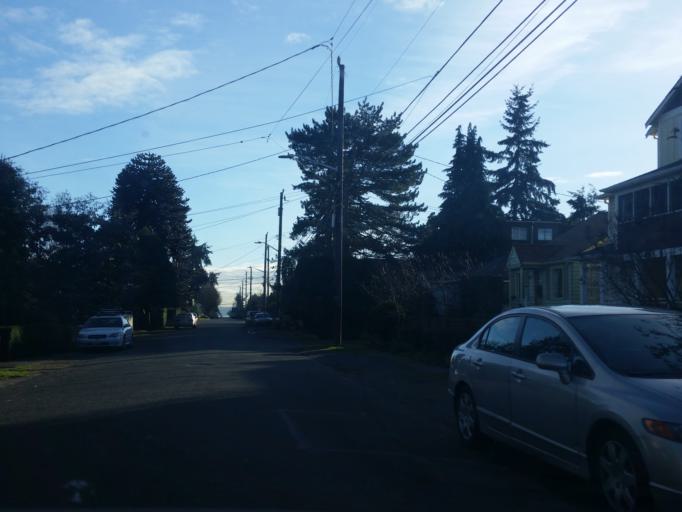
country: US
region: Washington
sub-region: King County
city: Shoreline
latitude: 47.6918
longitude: -122.3811
